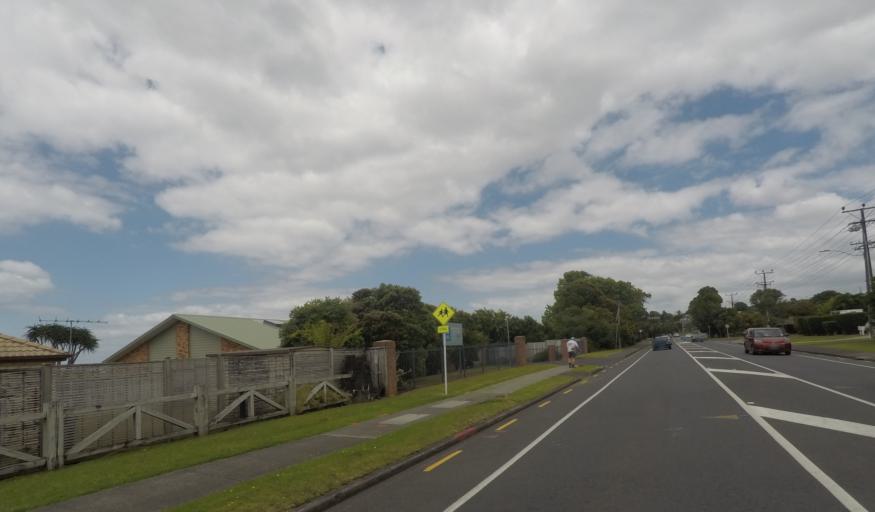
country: NZ
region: Auckland
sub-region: Auckland
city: Rosebank
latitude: -36.8261
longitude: 174.6077
